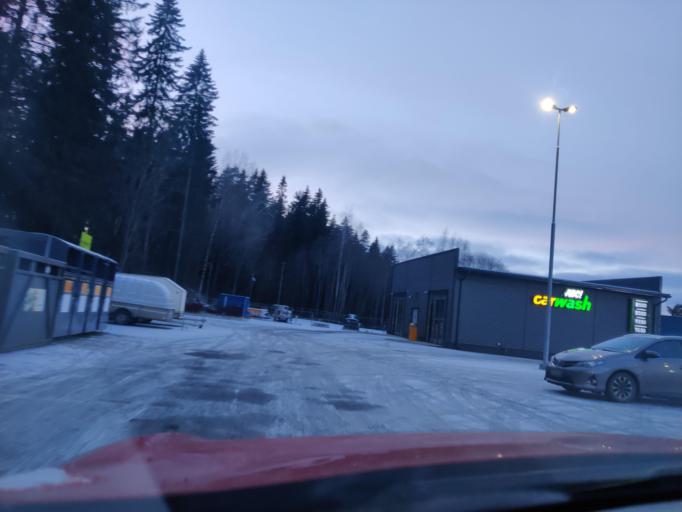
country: FI
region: Pirkanmaa
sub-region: Tampere
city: Nokia
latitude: 61.4776
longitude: 23.5241
